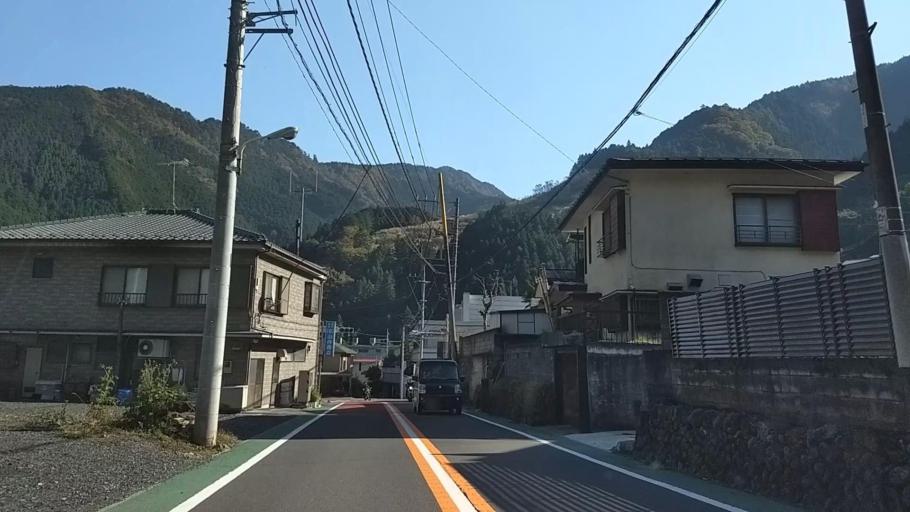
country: JP
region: Tokyo
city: Itsukaichi
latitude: 35.8013
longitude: 139.0881
